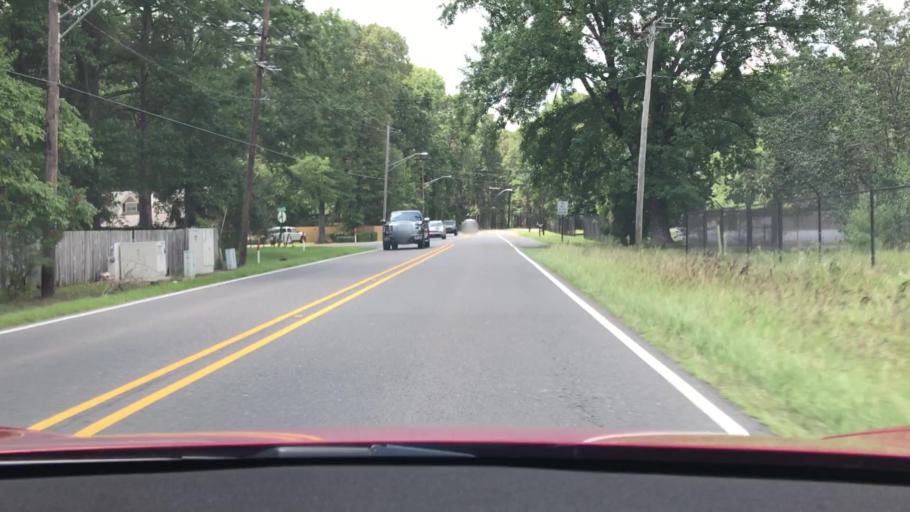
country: US
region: Louisiana
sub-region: Bossier Parish
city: Bossier City
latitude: 32.3905
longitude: -93.7225
